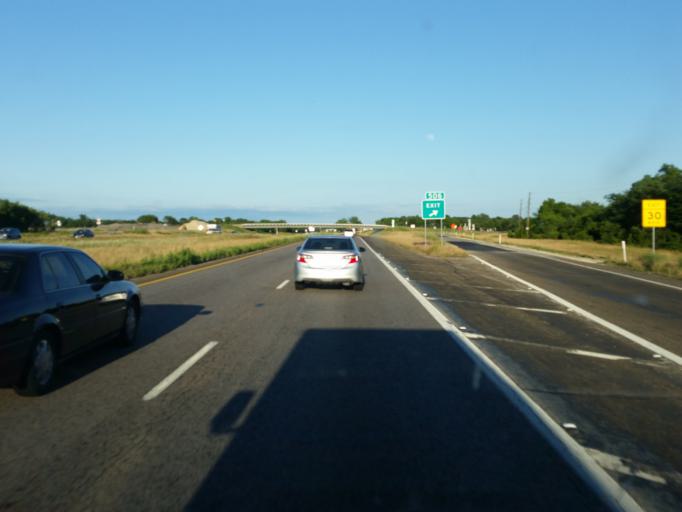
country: US
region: Texas
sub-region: Kaufman County
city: Terrell
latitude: 32.6822
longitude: -96.2003
